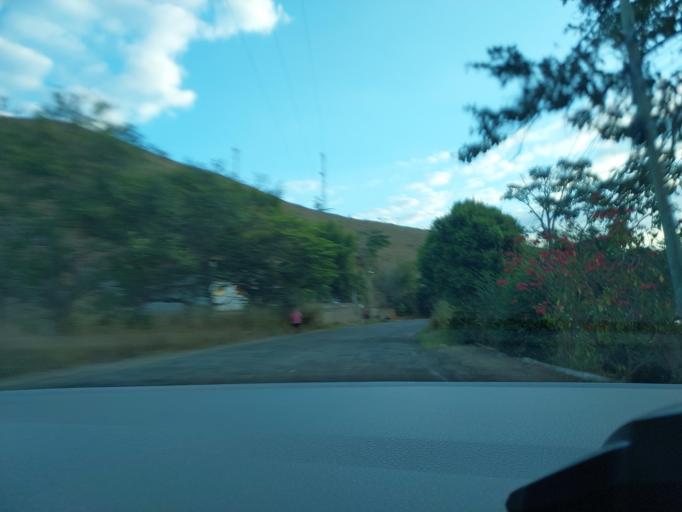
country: BR
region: Rio de Janeiro
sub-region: Natividade
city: Natividade
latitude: -21.1991
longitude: -42.1175
